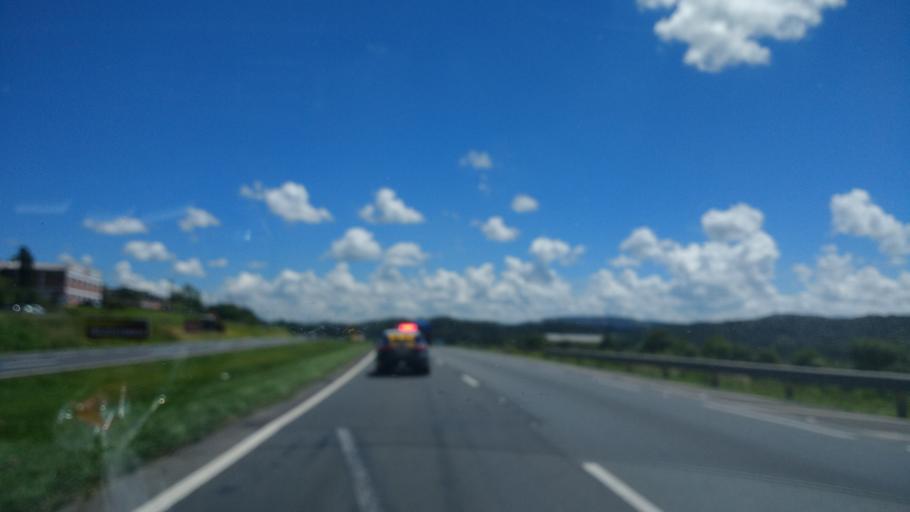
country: BR
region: Parana
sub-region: Campo Largo
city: Campo Largo
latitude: -25.4429
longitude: -49.5629
